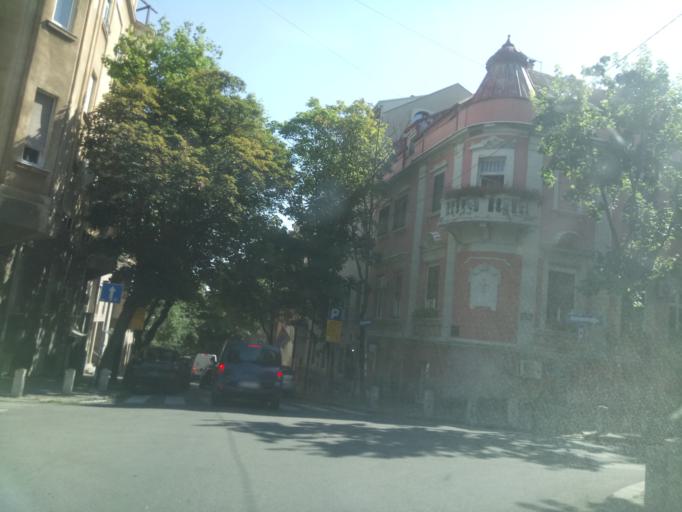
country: RS
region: Central Serbia
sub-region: Belgrade
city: Stari Grad
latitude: 44.8227
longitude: 20.4558
